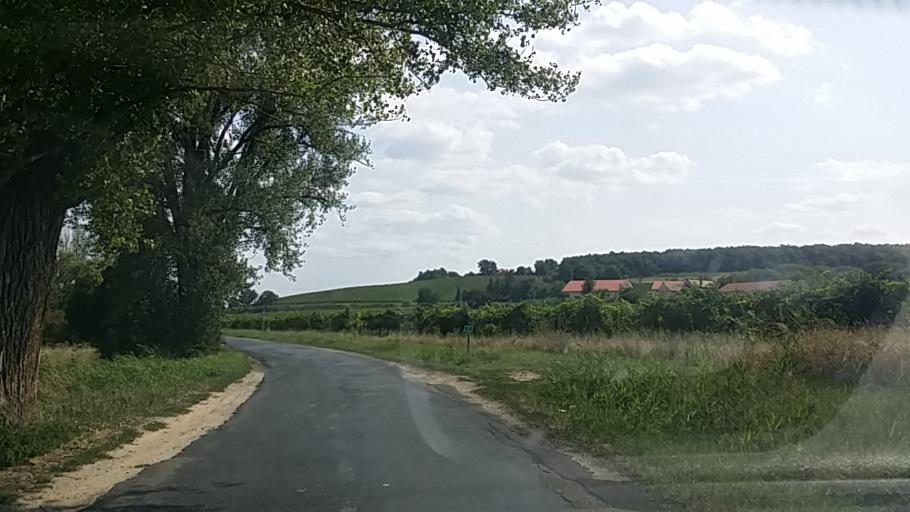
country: HU
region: Gyor-Moson-Sopron
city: Fertorakos
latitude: 47.6833
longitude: 16.6656
